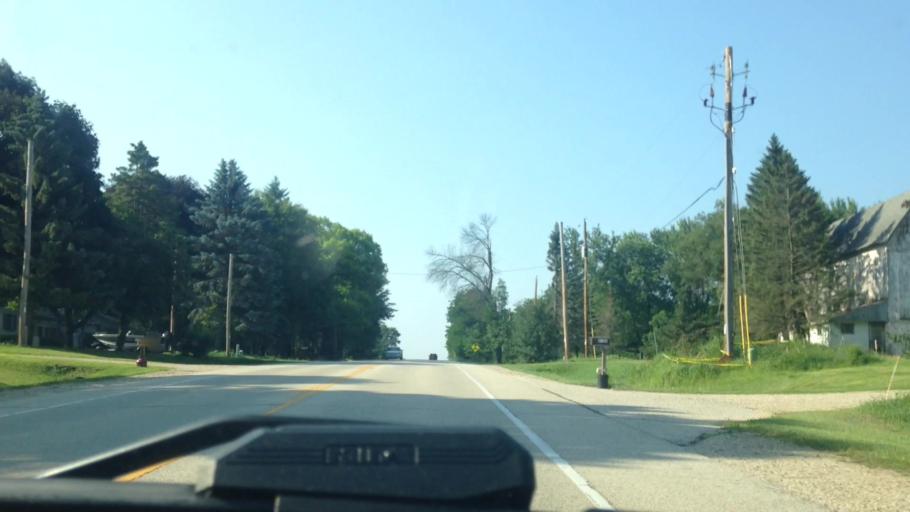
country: US
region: Wisconsin
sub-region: Washington County
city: Slinger
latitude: 43.3051
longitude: -88.2608
